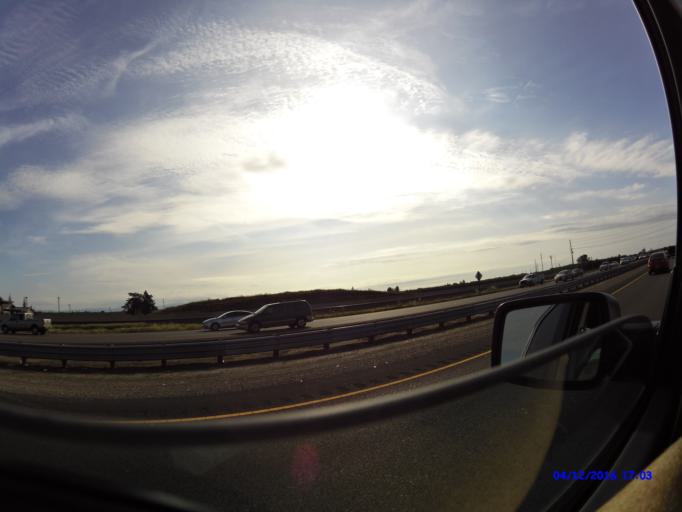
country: US
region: California
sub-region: Stanislaus County
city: Salida
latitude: 37.7195
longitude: -121.0968
